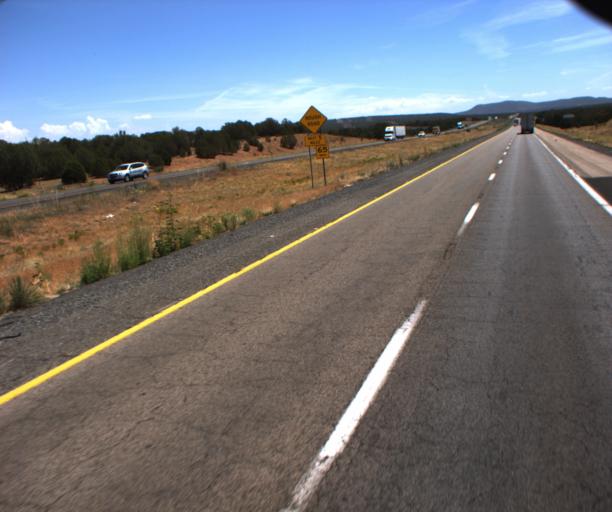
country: US
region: Arizona
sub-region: Mohave County
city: Peach Springs
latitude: 35.1907
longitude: -113.3584
